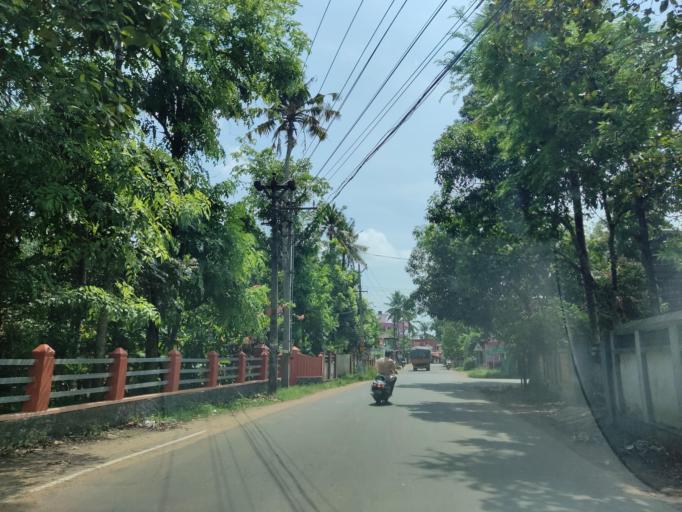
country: IN
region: Kerala
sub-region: Alappuzha
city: Chengannur
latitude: 9.3070
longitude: 76.5821
